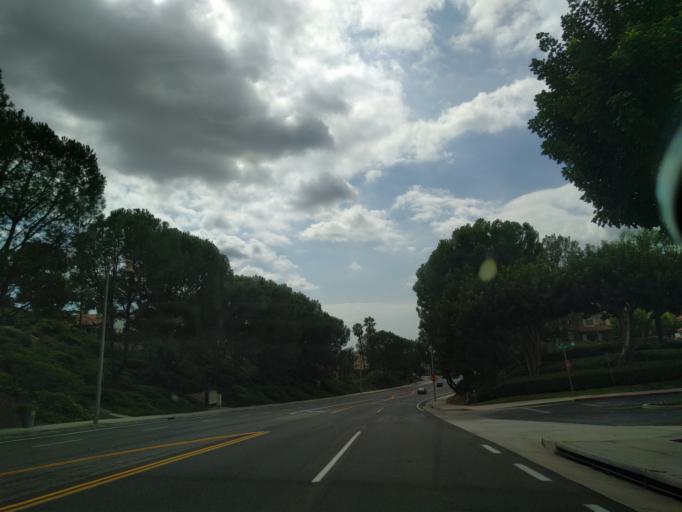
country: US
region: California
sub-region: Orange County
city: Portola Hills
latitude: 33.6574
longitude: -117.6392
